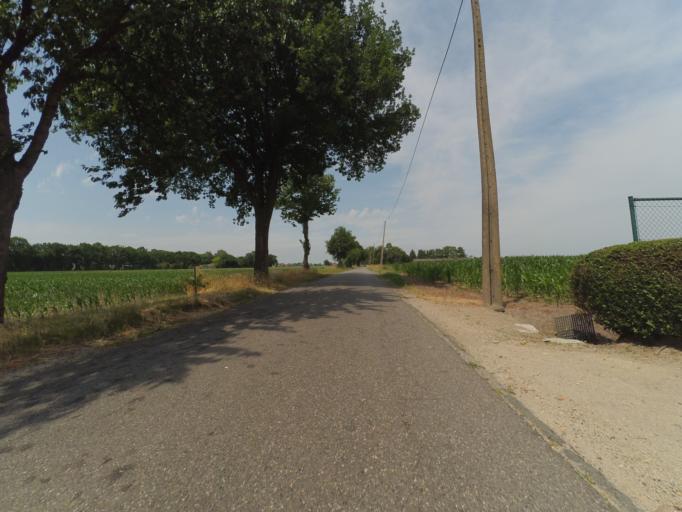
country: BE
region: Flanders
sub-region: Provincie Antwerpen
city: Essen
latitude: 51.4287
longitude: 4.4116
